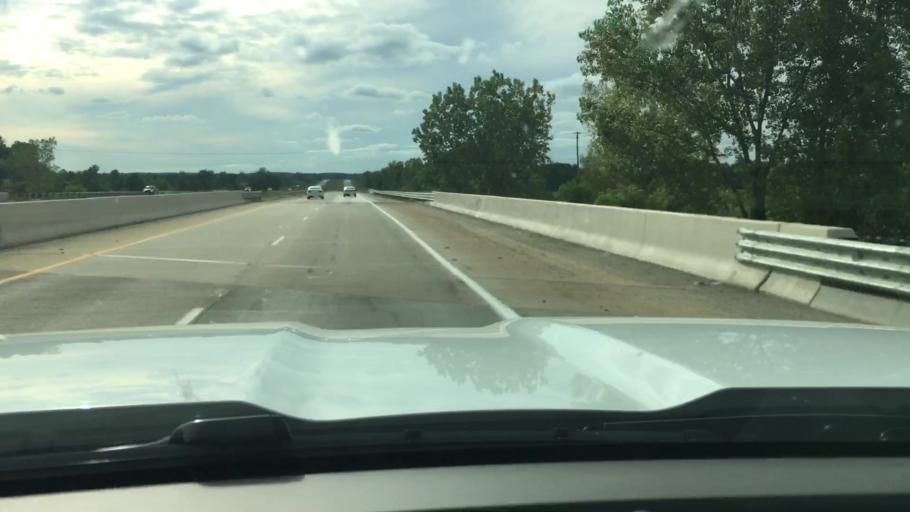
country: US
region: Michigan
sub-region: Lapeer County
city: Imlay City
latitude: 42.9977
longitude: -83.1024
